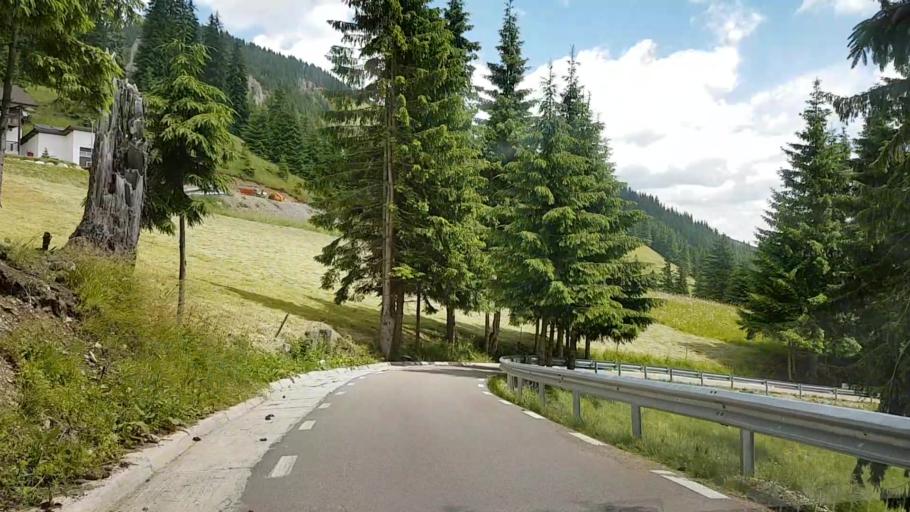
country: RO
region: Suceava
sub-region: Municipiul Campulung Moldovenesc
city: Campulung Moldovenesc
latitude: 47.4377
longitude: 25.5517
